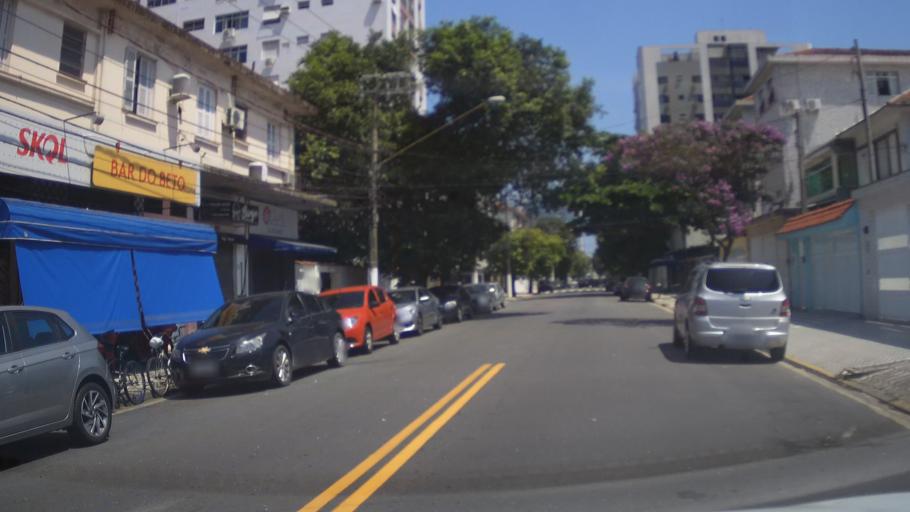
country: BR
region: Sao Paulo
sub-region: Santos
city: Santos
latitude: -23.9706
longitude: -46.3032
